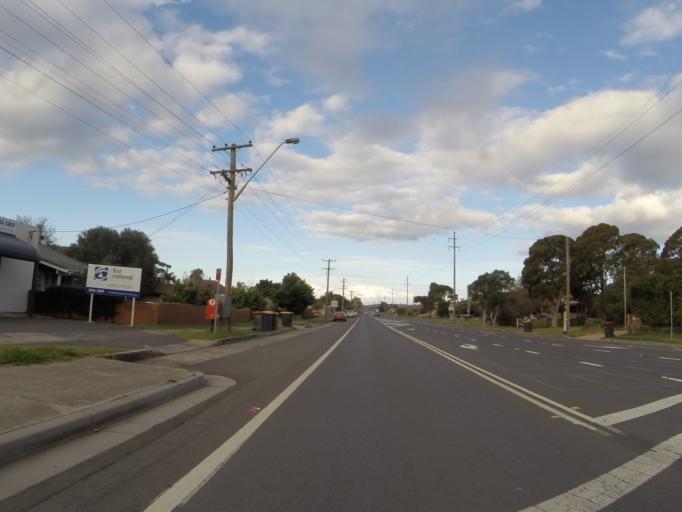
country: AU
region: New South Wales
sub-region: Shellharbour
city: Albion Park Rail
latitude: -34.5715
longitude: 150.7658
